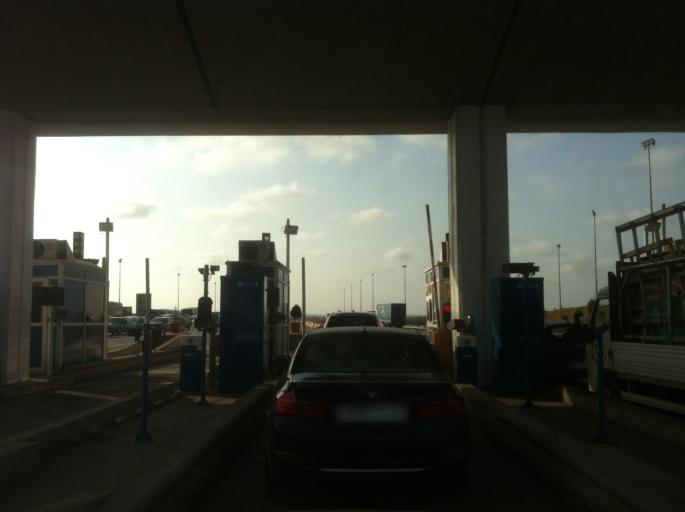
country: MA
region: Gharb-Chrarda-Beni Hssen
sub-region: Kenitra Province
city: Kenitra
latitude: 34.2281
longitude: -6.5256
